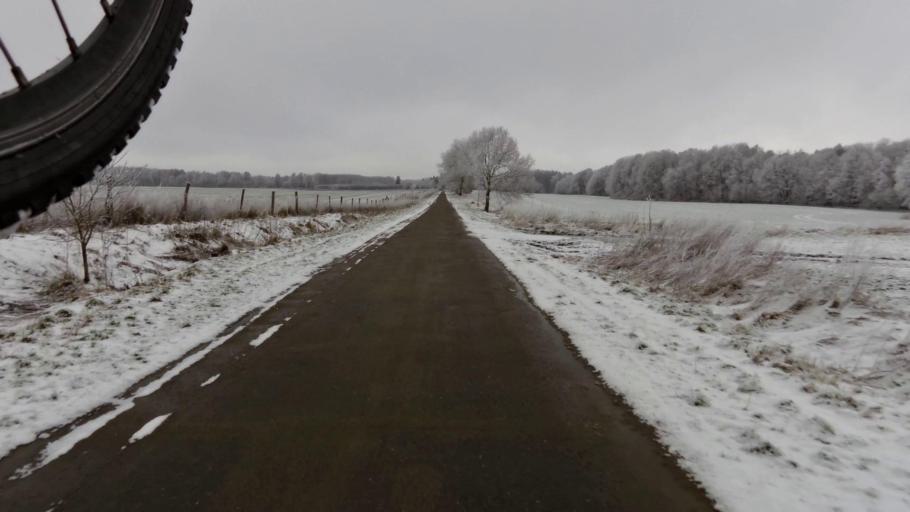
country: PL
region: West Pomeranian Voivodeship
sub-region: Powiat swidwinski
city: Rabino
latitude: 53.8173
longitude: 15.9733
